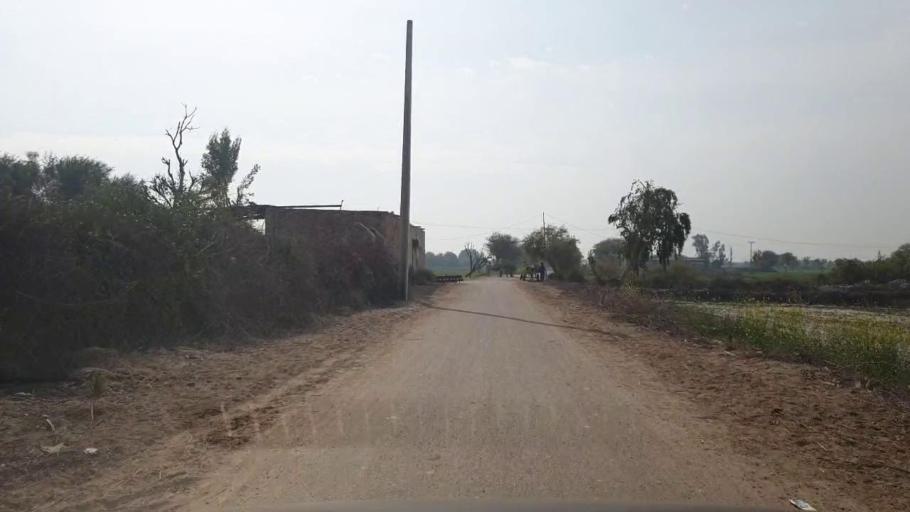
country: PK
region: Sindh
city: Hala
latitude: 25.9874
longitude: 68.4228
